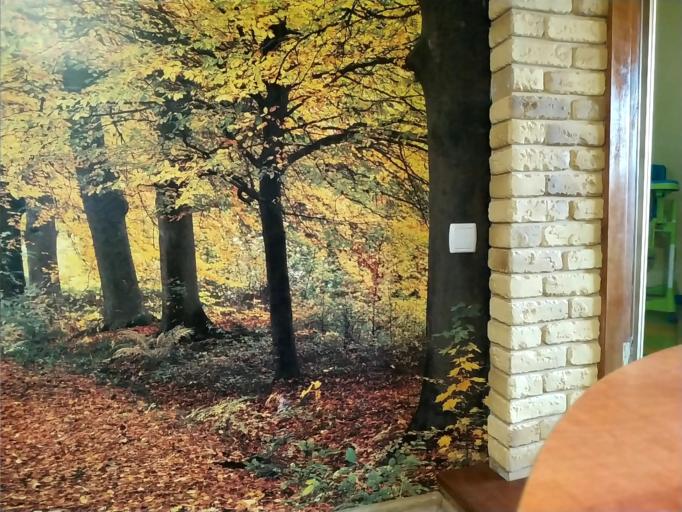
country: RU
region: Leningrad
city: Tolmachevo
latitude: 58.9473
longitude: 29.6455
